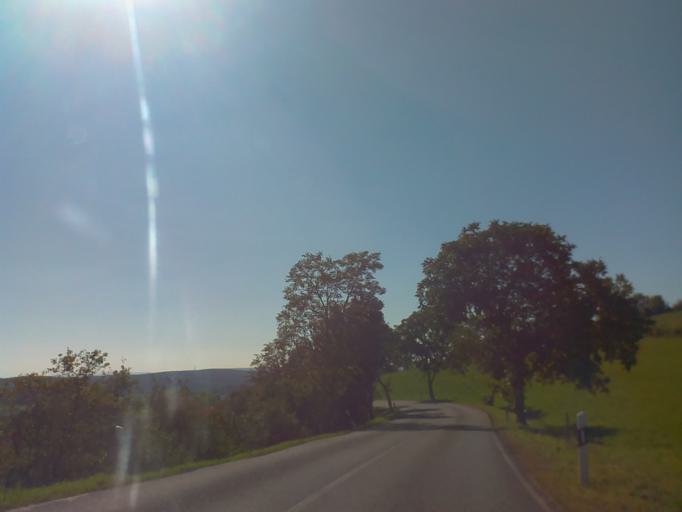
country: DE
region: Thuringia
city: Seitenroda
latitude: 50.7999
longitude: 11.6140
